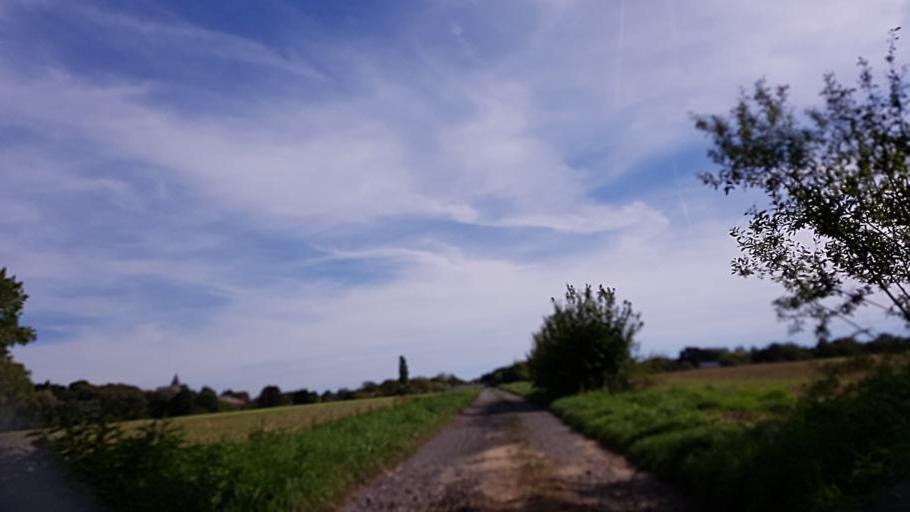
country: BE
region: Wallonia
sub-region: Province du Brabant Wallon
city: Beauvechain
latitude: 50.7771
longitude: 4.7364
